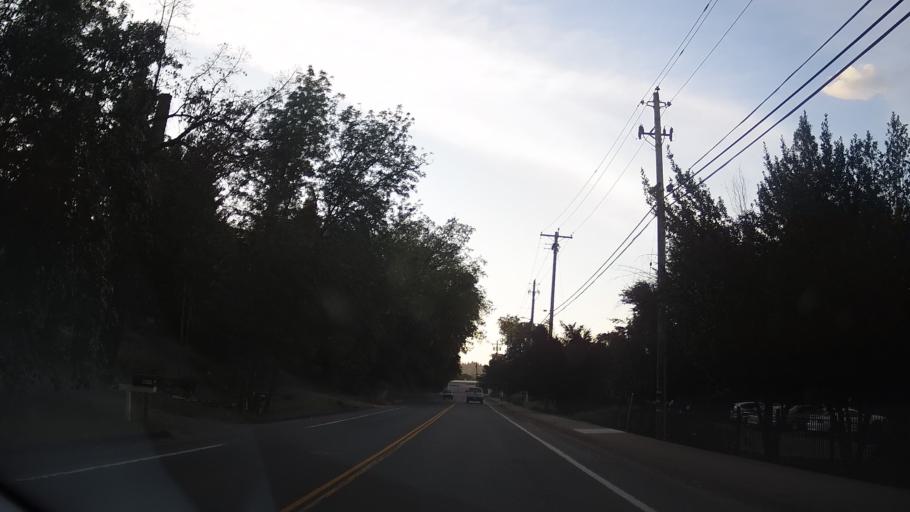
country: US
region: California
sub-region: Mendocino County
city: Willits
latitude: 39.3946
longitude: -123.3438
